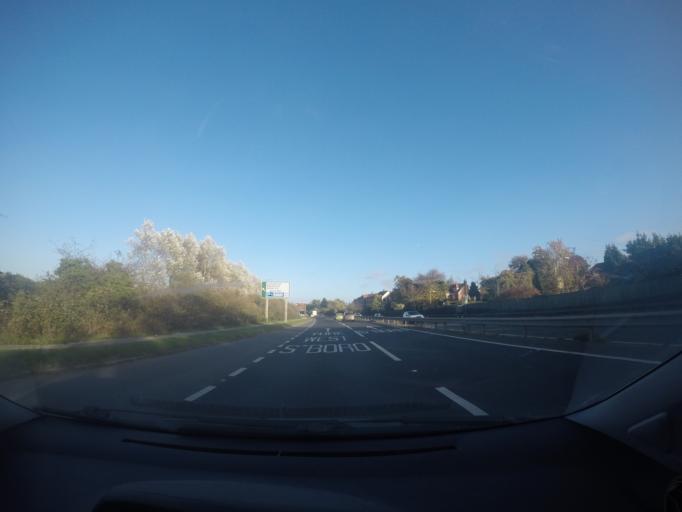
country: GB
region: England
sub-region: City of York
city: Copmanthorpe
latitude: 53.9208
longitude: -1.1416
